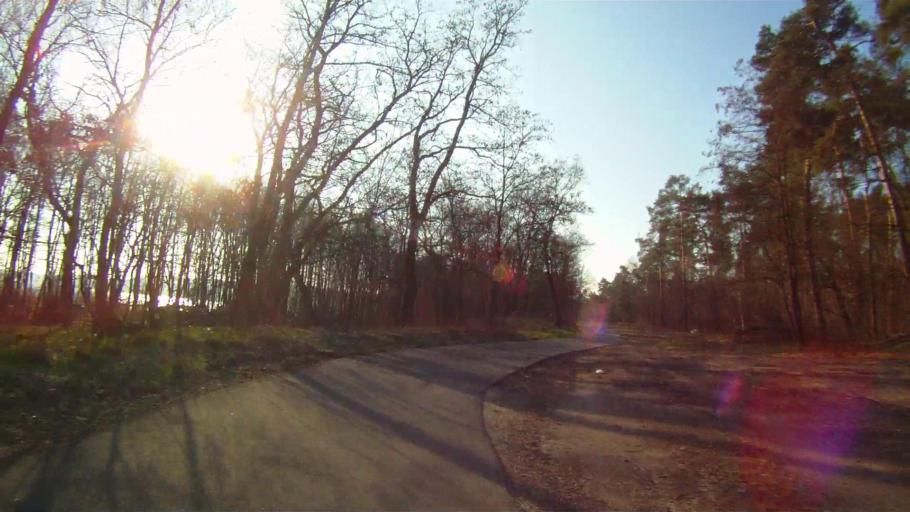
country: DE
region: Berlin
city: Friedrichshagen
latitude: 52.4352
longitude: 13.6196
